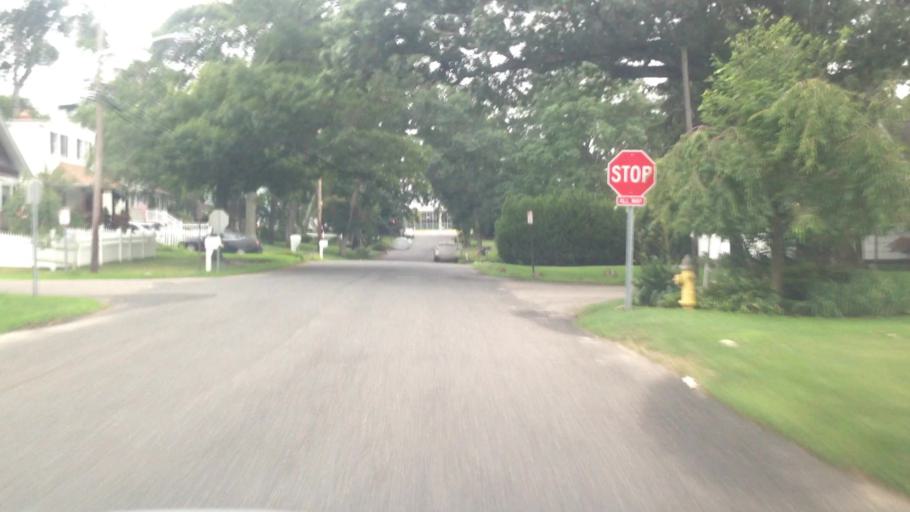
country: US
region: New York
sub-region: Suffolk County
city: Lake Grove
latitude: 40.8415
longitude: -73.1024
